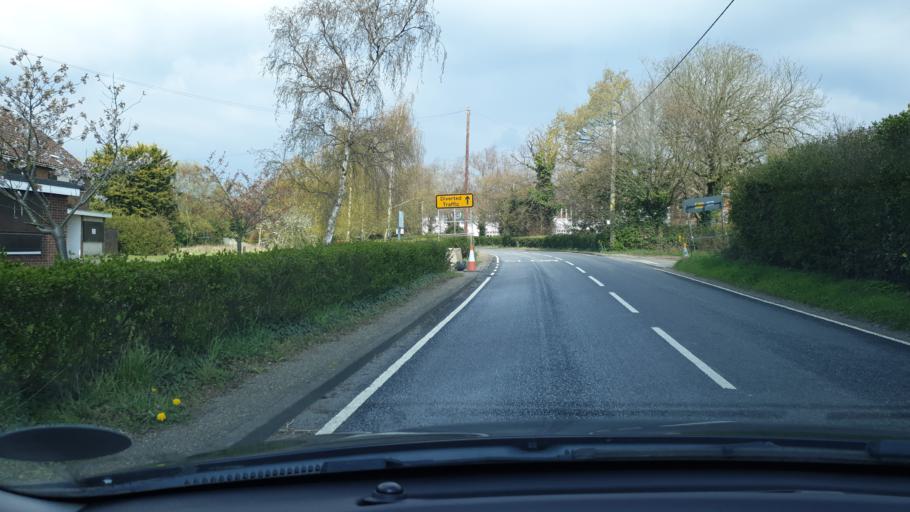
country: GB
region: England
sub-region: Essex
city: Mistley
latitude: 51.8941
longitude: 1.1022
